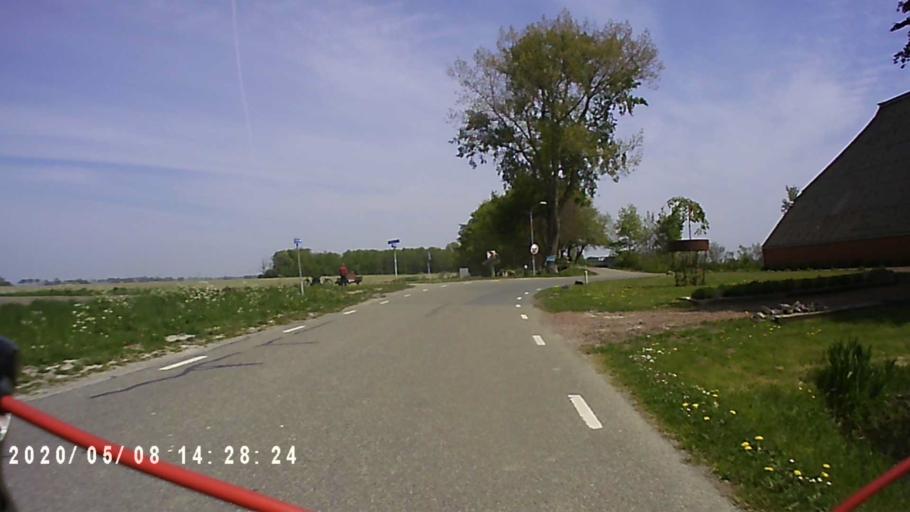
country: NL
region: Groningen
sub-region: Gemeente Appingedam
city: Appingedam
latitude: 53.3614
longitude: 6.7791
